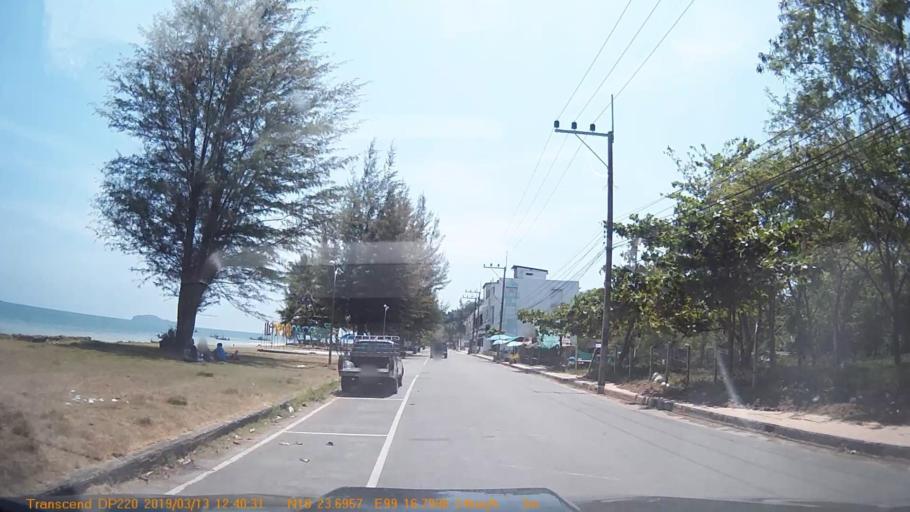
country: TH
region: Chumphon
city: Chumphon
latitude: 10.3948
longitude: 99.2800
